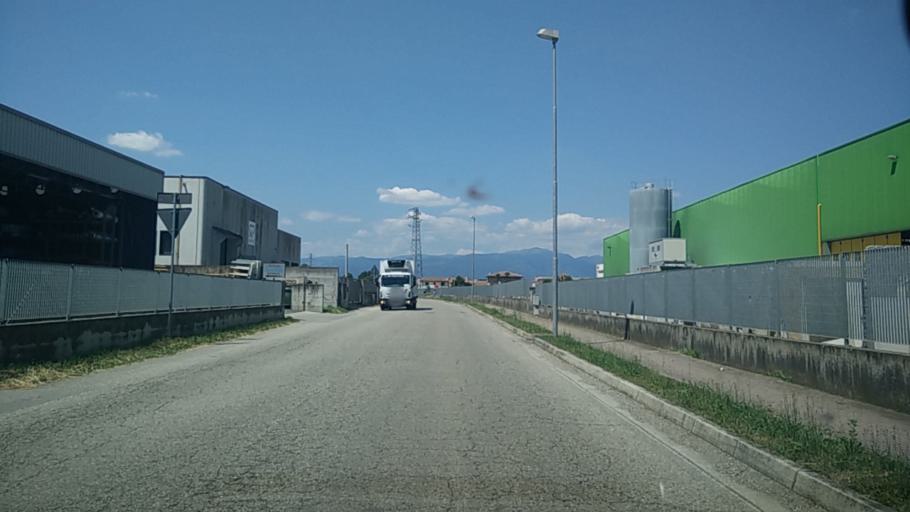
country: IT
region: Veneto
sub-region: Provincia di Padova
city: Tombolo
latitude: 45.6420
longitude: 11.8123
